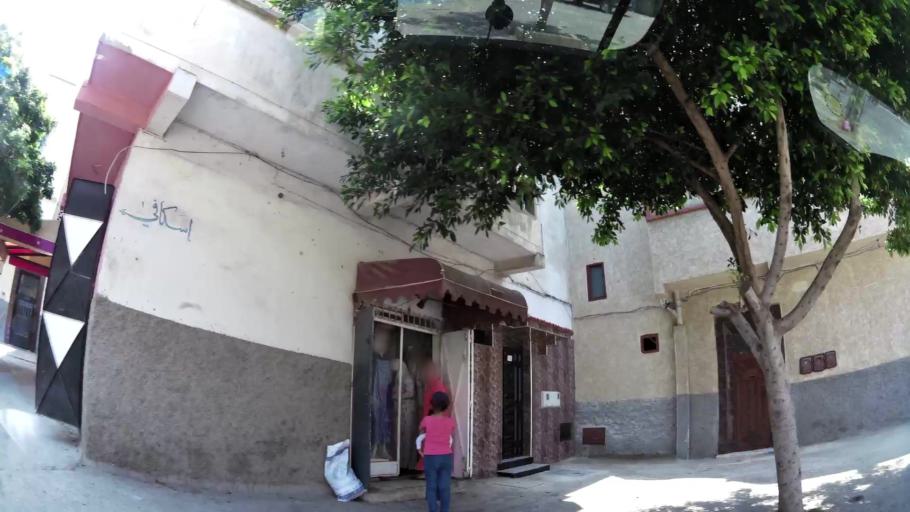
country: MA
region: Rabat-Sale-Zemmour-Zaer
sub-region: Rabat
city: Rabat
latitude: 33.9813
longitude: -6.8803
